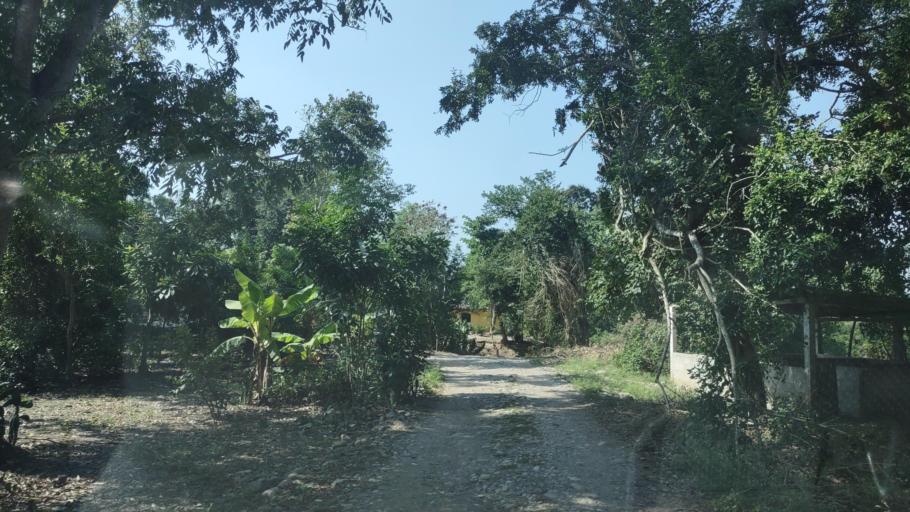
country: MX
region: Puebla
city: Espinal
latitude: 20.2518
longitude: -97.3383
